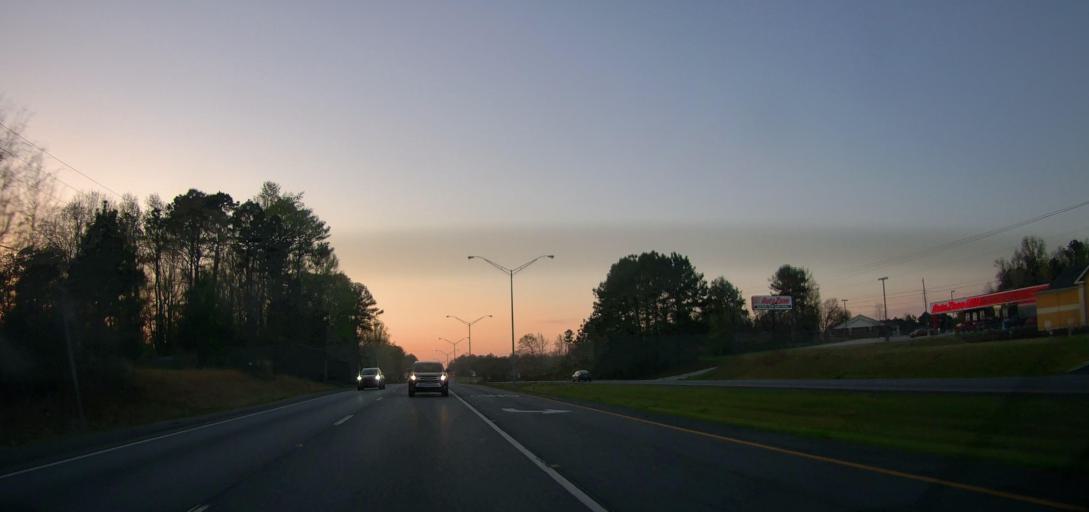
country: US
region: Alabama
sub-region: Tallapoosa County
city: Alexander City
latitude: 32.9353
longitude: -85.9734
